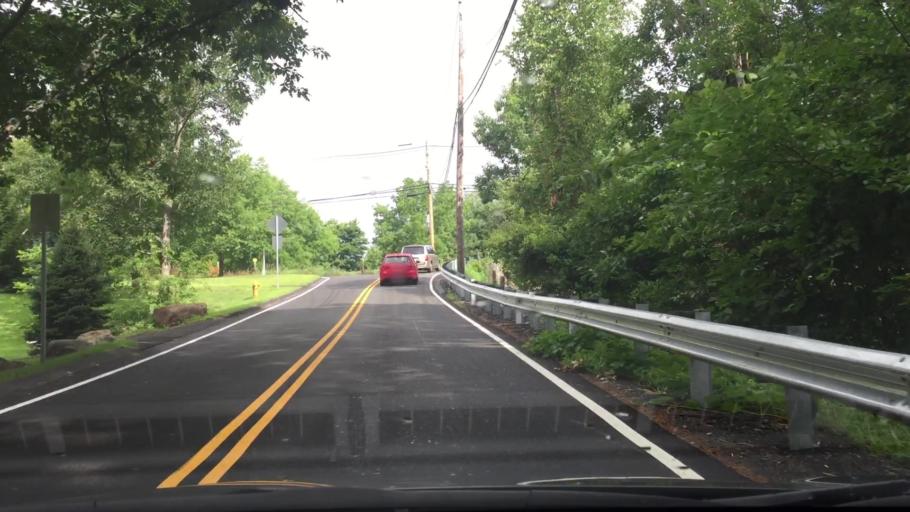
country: US
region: Massachusetts
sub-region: Middlesex County
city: Littleton Common
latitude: 42.5232
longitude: -71.4597
